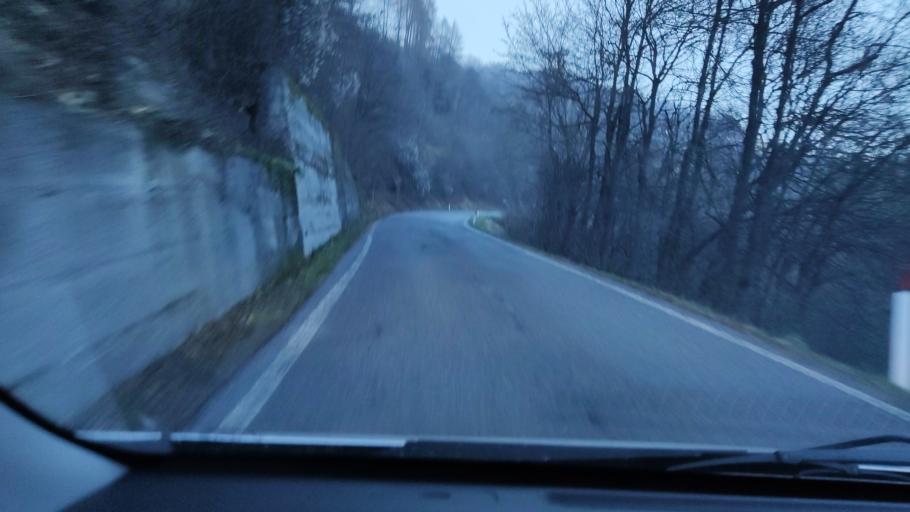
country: IT
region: Piedmont
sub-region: Provincia di Cuneo
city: Viola
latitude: 44.2888
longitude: 7.9754
